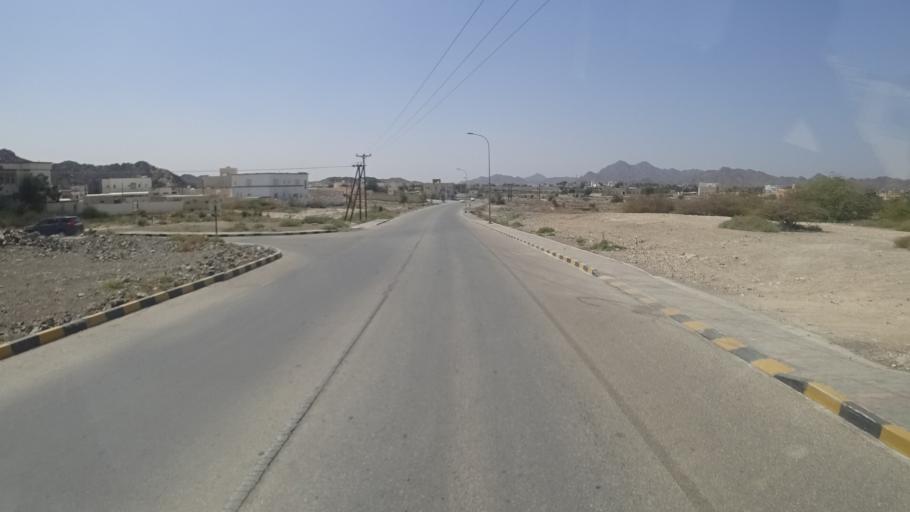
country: OM
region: Ash Sharqiyah
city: Ibra'
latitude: 22.6816
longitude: 58.5403
